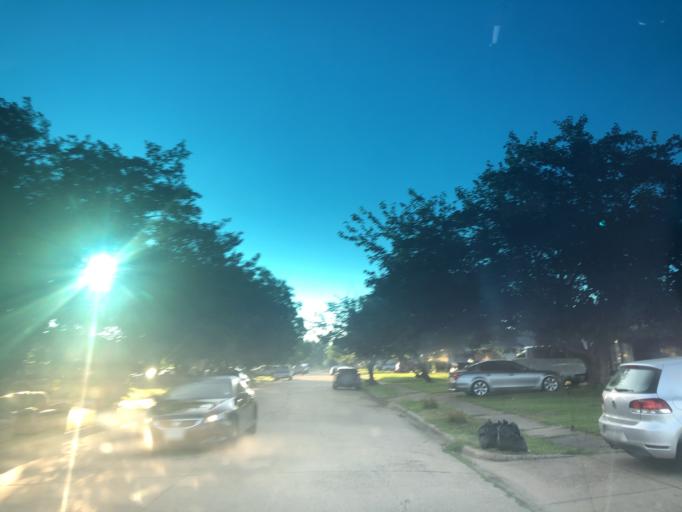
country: US
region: Texas
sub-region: Dallas County
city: Grand Prairie
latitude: 32.7026
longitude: -97.0110
